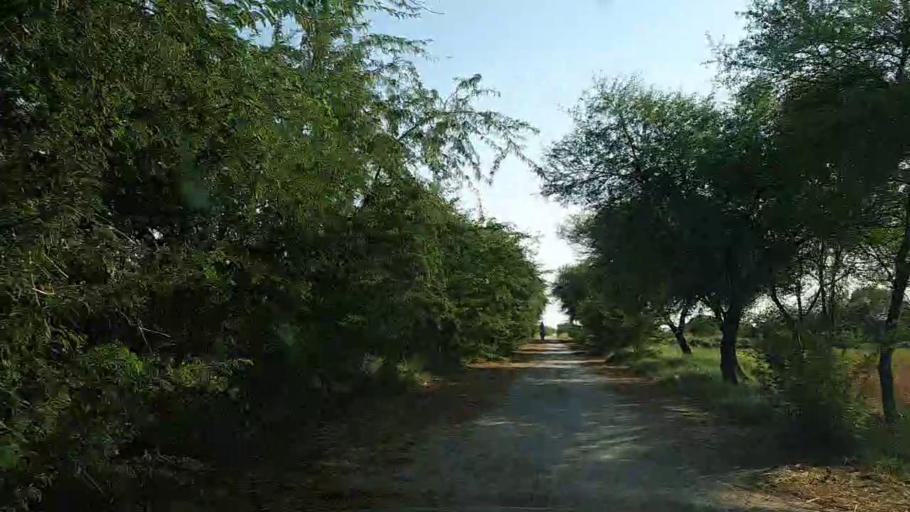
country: PK
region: Sindh
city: Daro Mehar
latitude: 24.6455
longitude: 68.0751
